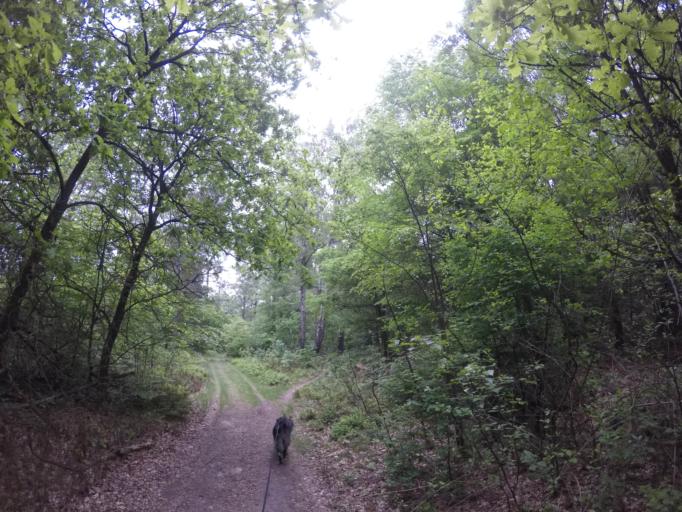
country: NL
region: Gelderland
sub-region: Gemeente Rozendaal
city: Rozendaal
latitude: 52.0208
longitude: 5.9844
